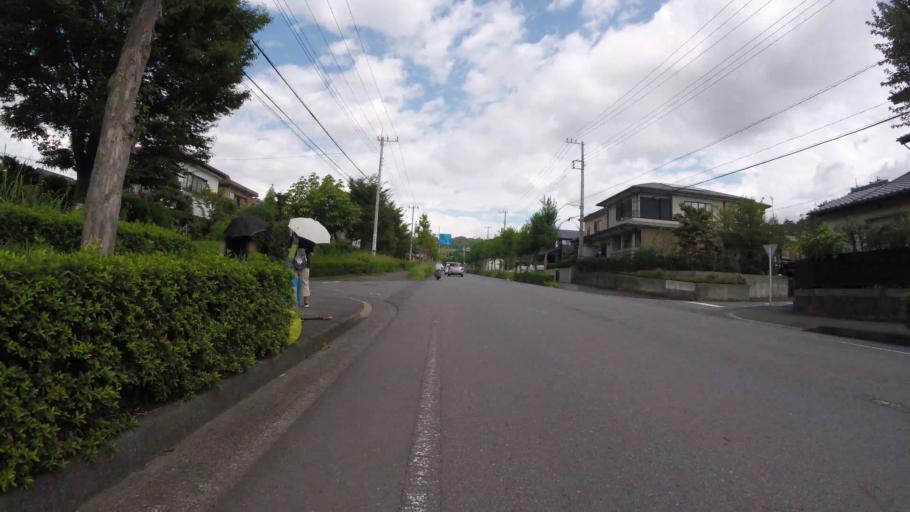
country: JP
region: Shizuoka
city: Mishima
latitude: 35.1358
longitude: 138.9332
